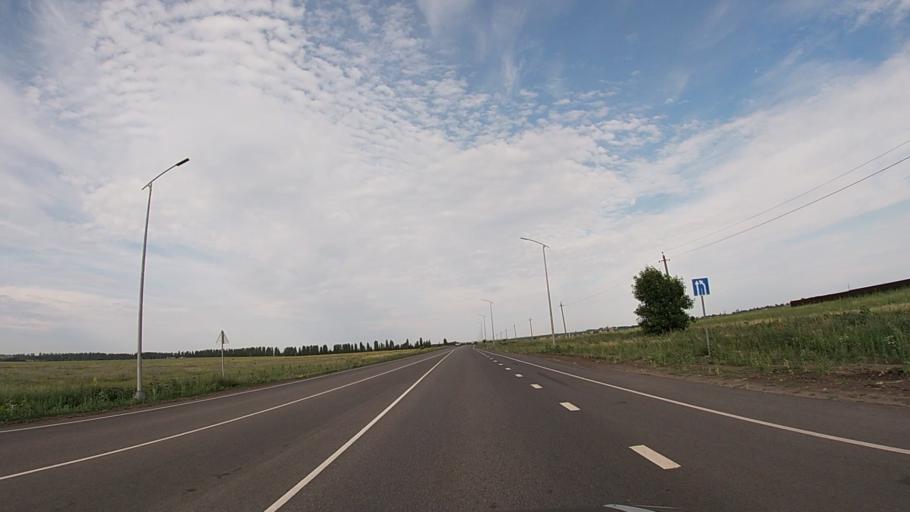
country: RU
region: Belgorod
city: Severnyy
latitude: 50.6665
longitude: 36.5389
